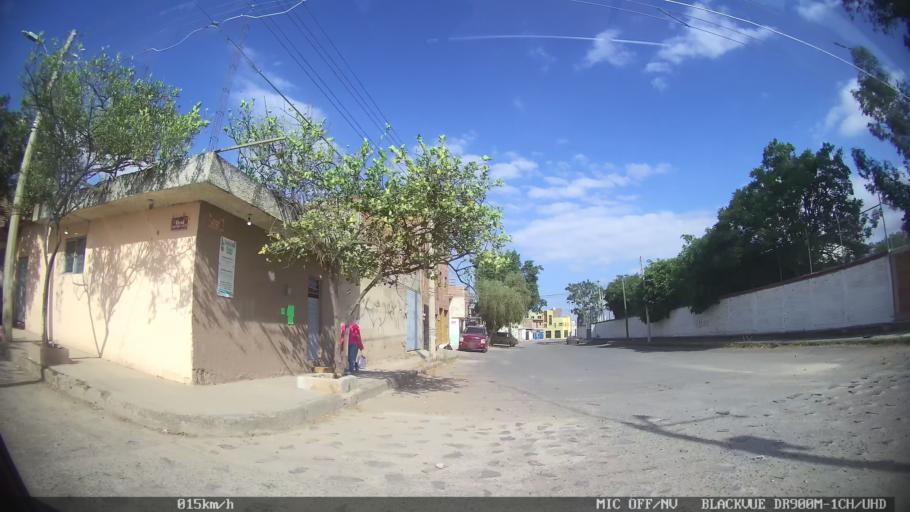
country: MX
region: Jalisco
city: Tonala
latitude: 20.6518
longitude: -103.2474
